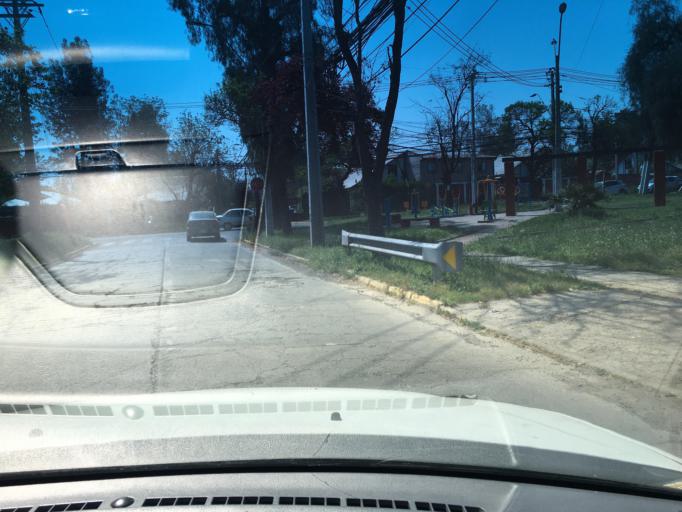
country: CL
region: Santiago Metropolitan
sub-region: Provincia de Santiago
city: Villa Presidente Frei, Nunoa, Santiago, Chile
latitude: -33.5189
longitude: -70.5649
